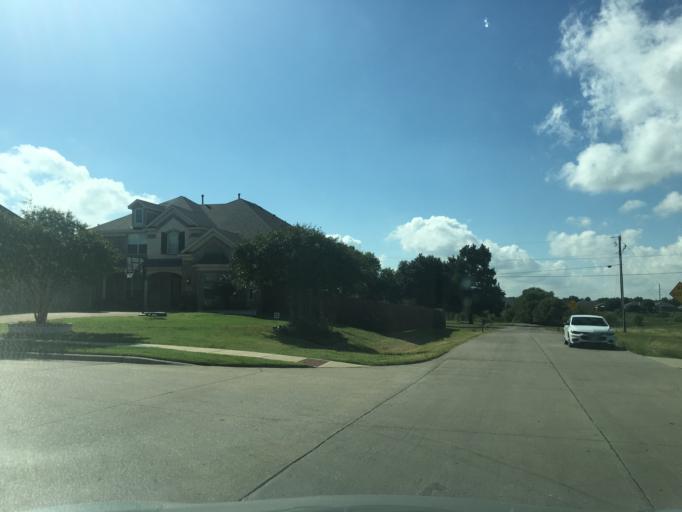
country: US
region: Texas
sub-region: Dallas County
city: Sachse
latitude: 32.9697
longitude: -96.5791
